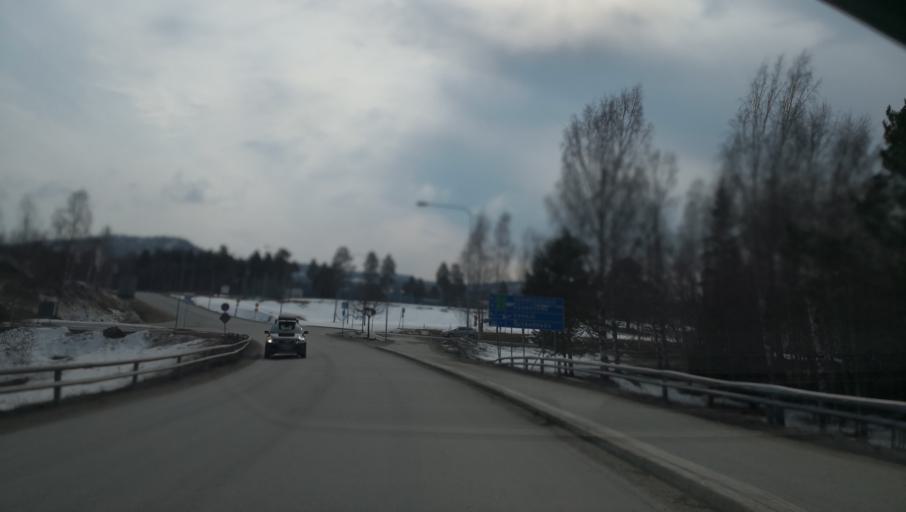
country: SE
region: Vaesternorrland
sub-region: OErnskoeldsviks Kommun
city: Ornskoldsvik
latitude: 63.2904
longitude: 18.6102
